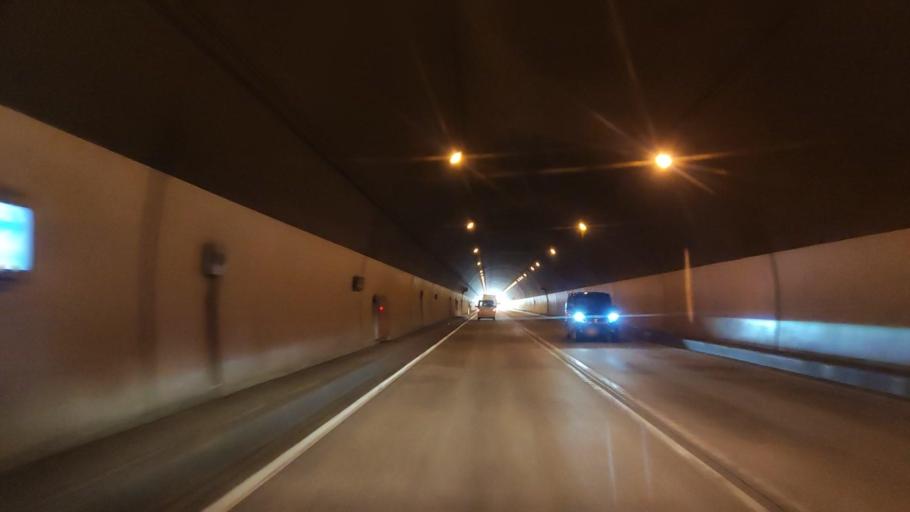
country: JP
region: Yamagata
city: Kaminoyama
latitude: 38.0978
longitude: 140.2013
